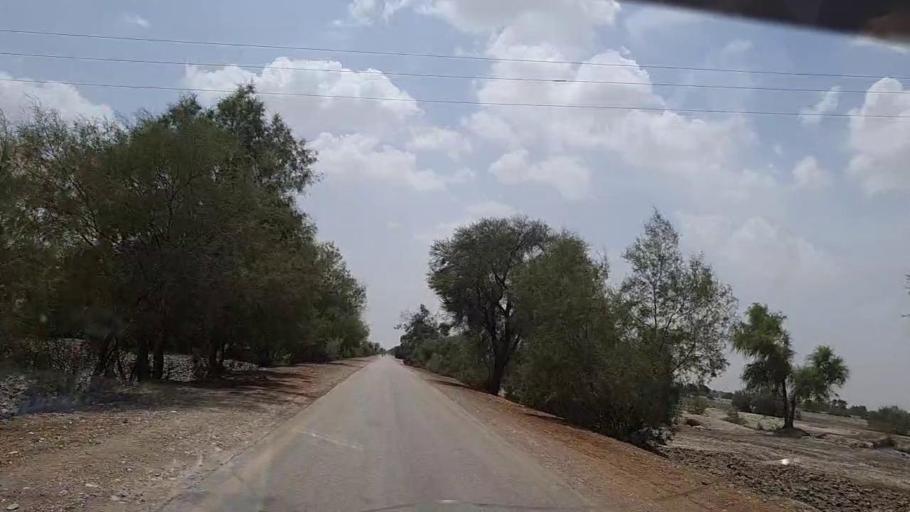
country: PK
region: Sindh
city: Bhan
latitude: 26.5412
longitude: 67.6572
